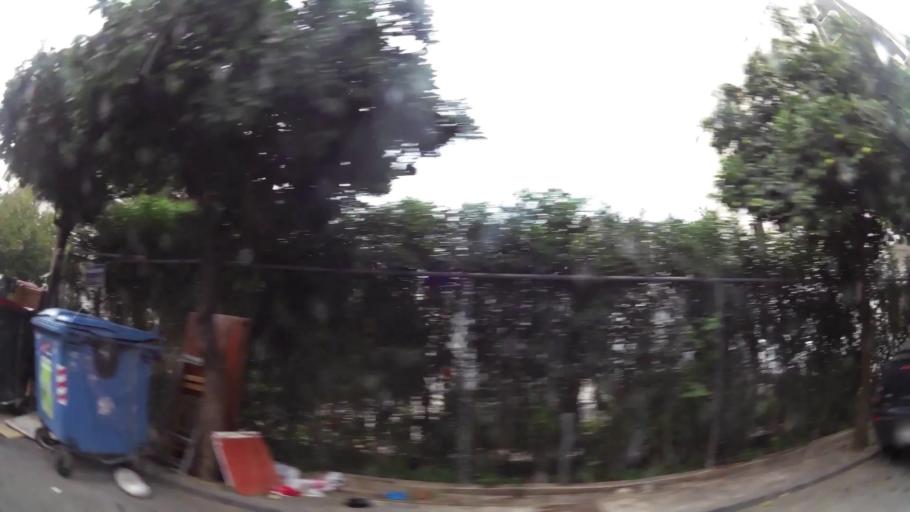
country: GR
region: Attica
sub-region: Nomos Piraios
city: Agios Ioannis Rentis
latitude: 37.9570
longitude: 23.6721
